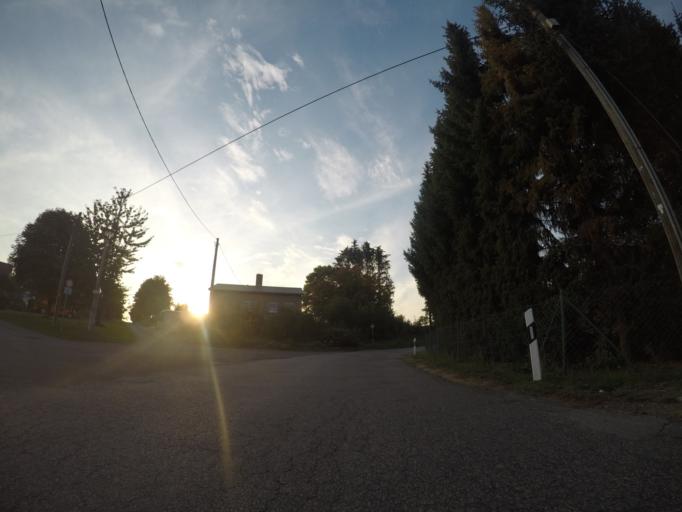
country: DE
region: Thuringia
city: Altkirchen
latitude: 50.9202
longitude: 12.3360
